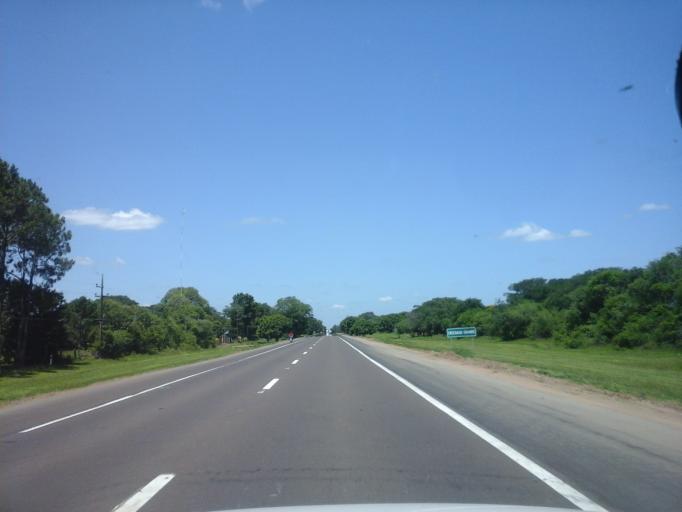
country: AR
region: Corrientes
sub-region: Departamento de San Cosme
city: San Cosme
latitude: -27.3680
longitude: -58.4002
